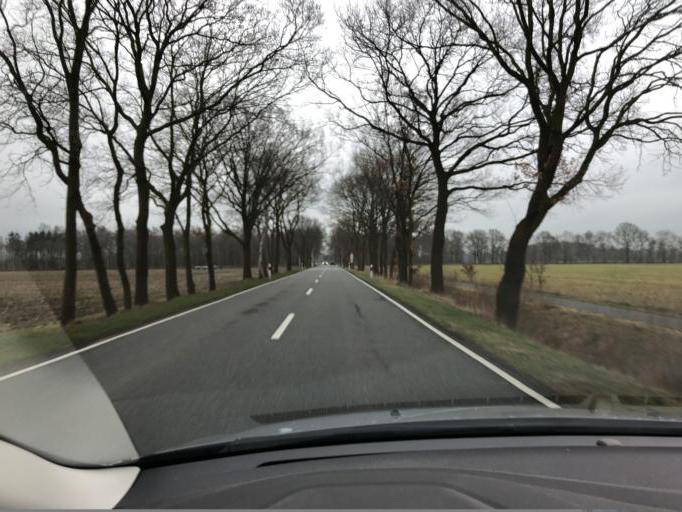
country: DE
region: Lower Saxony
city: Oldenburg
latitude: 53.1279
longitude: 8.3007
